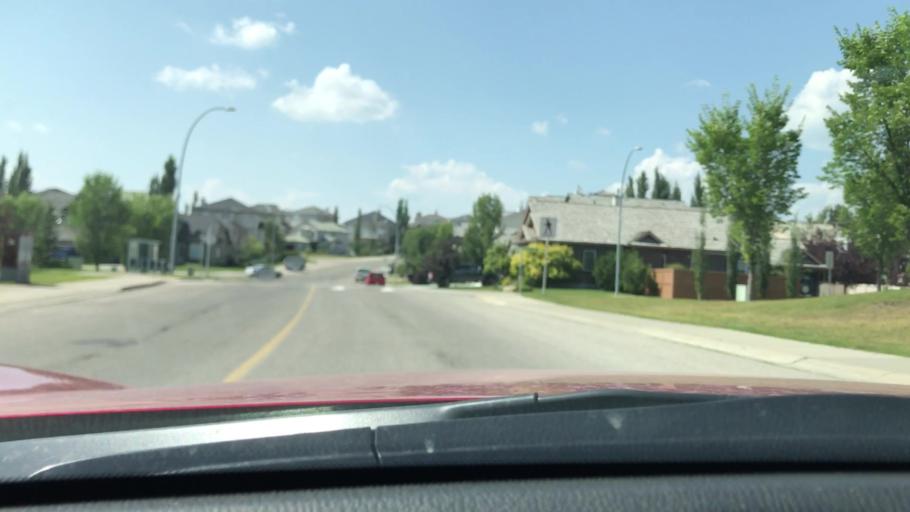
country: CA
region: Alberta
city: Calgary
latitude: 51.0266
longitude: -114.1784
